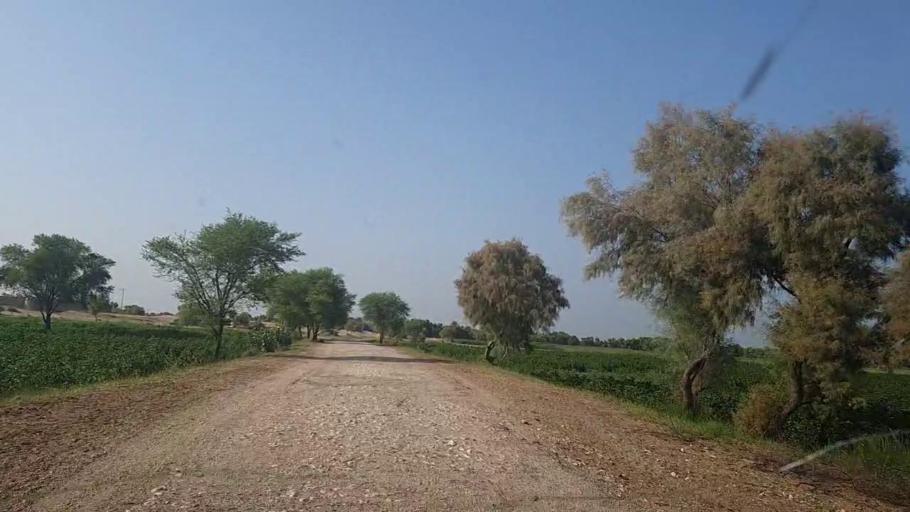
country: PK
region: Sindh
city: Khanpur
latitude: 27.7208
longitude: 69.3318
